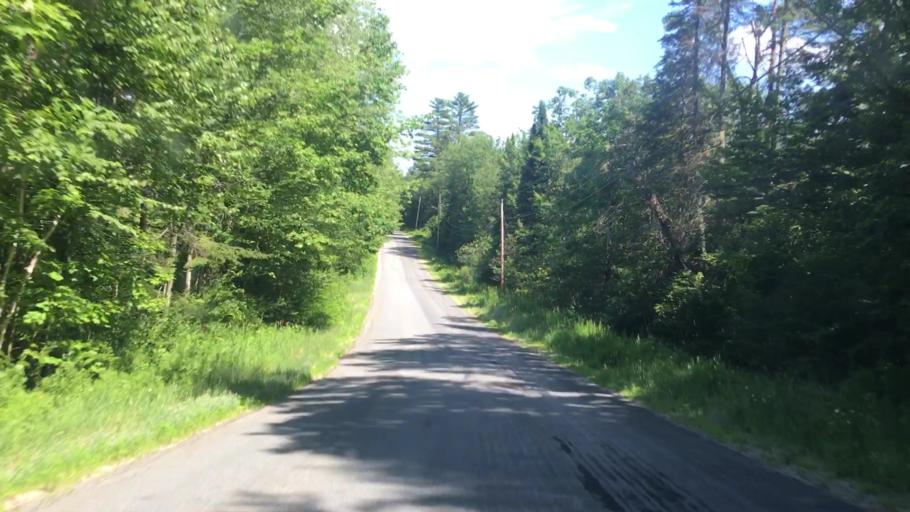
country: US
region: Maine
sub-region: Franklin County
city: Chesterville
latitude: 44.5558
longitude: -70.1119
